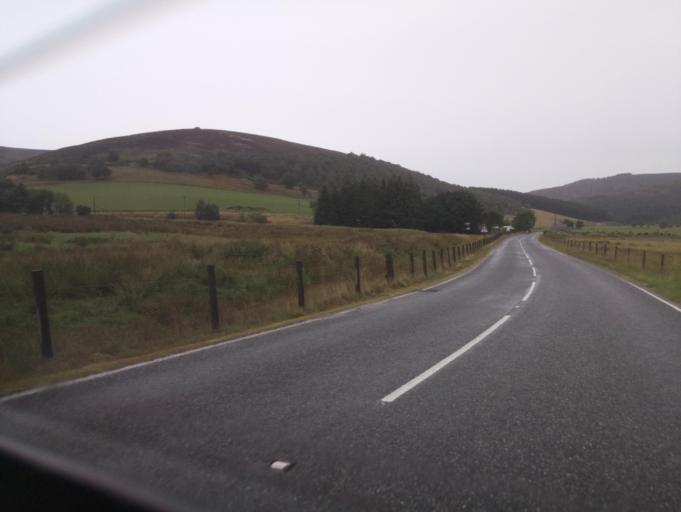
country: GB
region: Scotland
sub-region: Aberdeenshire
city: Ballater
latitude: 57.1615
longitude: -3.1885
